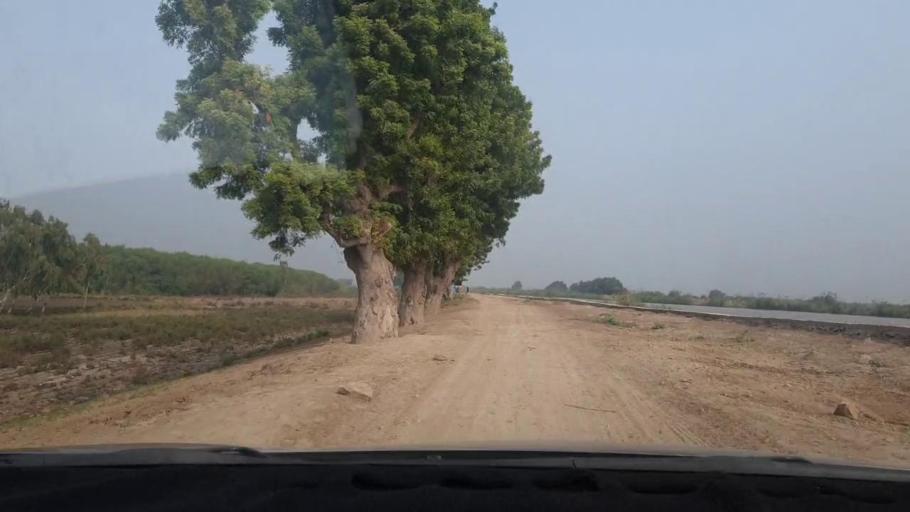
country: PK
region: Sindh
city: Matiari
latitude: 25.6507
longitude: 68.5613
